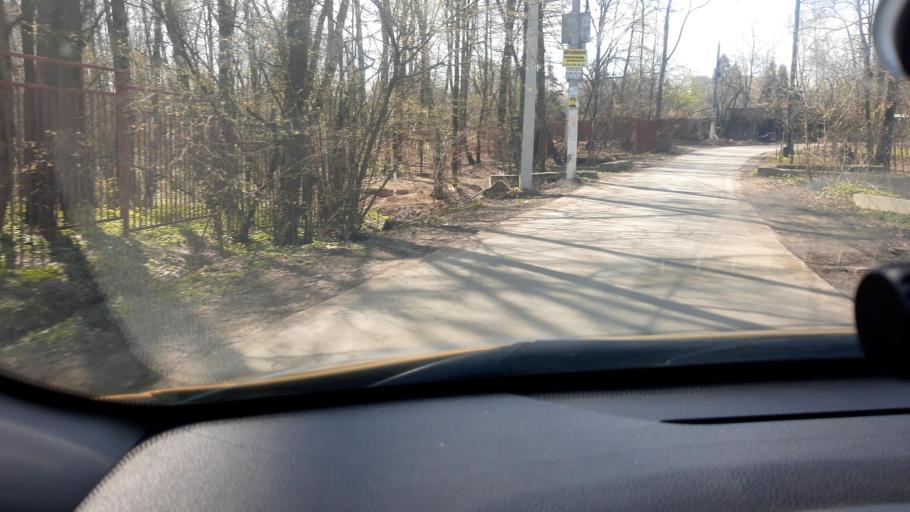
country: RU
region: Moscow
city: Annino
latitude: 55.5333
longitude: 37.6017
